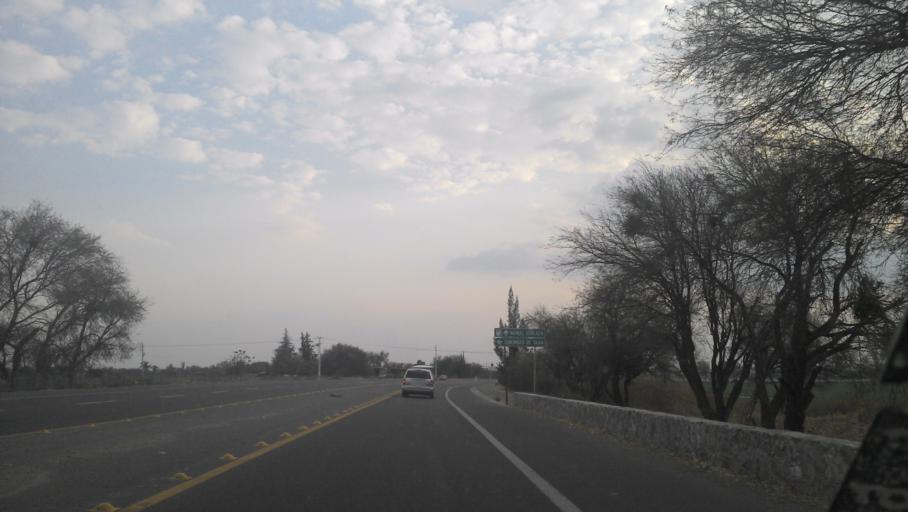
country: MX
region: Guanajuato
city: San Roque
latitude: 20.9575
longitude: -101.8981
